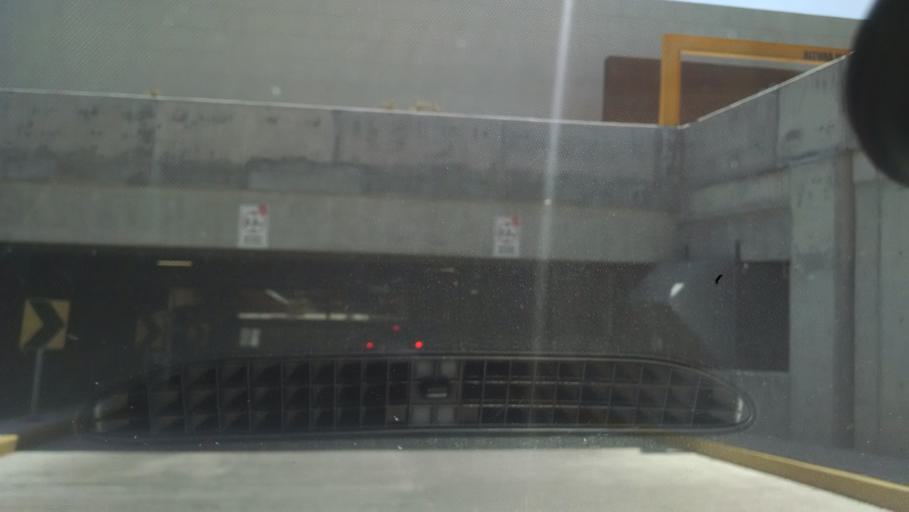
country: MX
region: Guanajuato
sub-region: Leon
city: La Ermita
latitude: 21.1590
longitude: -101.6966
